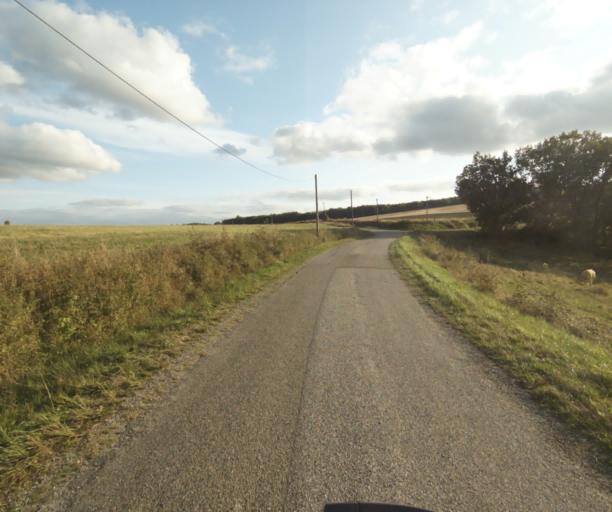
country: FR
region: Midi-Pyrenees
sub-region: Departement de la Haute-Garonne
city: Launac
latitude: 43.8175
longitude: 1.1359
